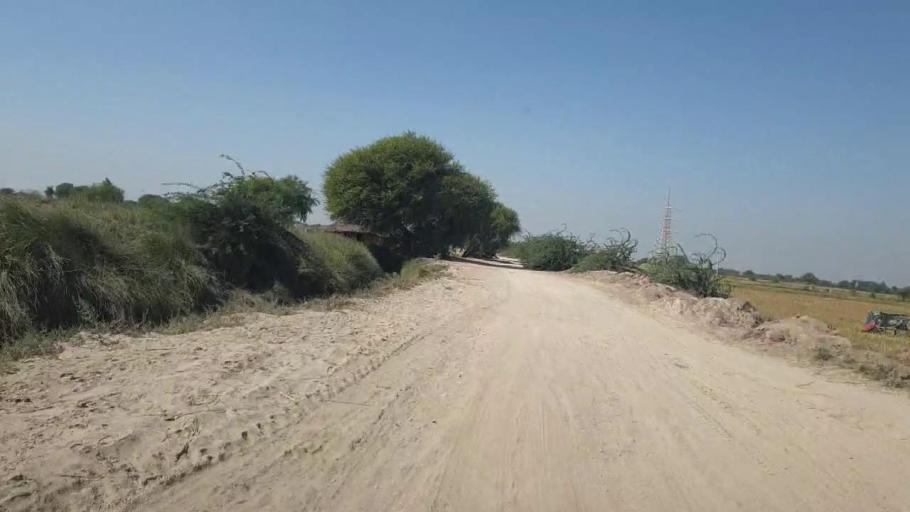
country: PK
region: Sindh
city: Talhar
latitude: 24.8343
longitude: 68.8117
